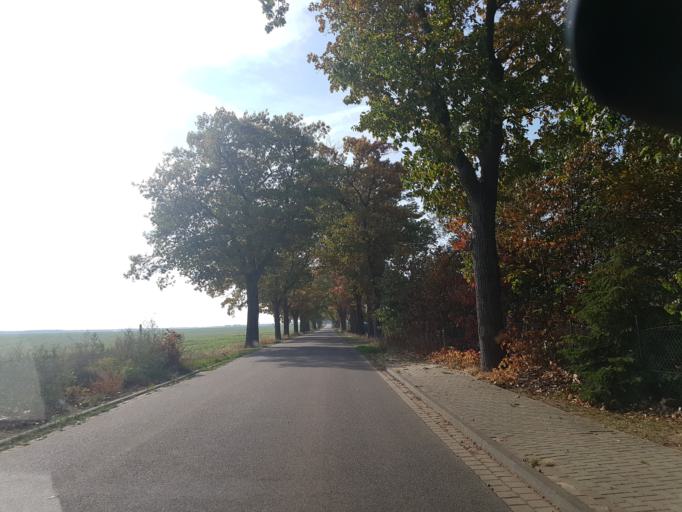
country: DE
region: Brandenburg
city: Ihlow
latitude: 51.8986
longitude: 13.2531
